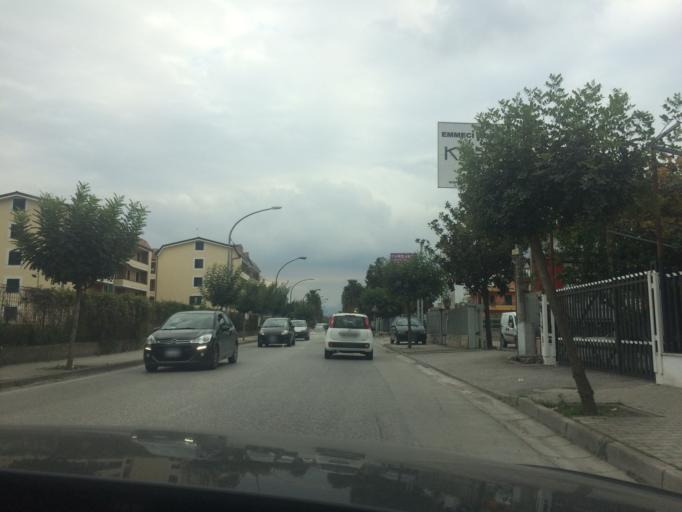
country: IT
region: Campania
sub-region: Provincia di Napoli
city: Palma Campania
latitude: 40.8700
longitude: 14.5471
